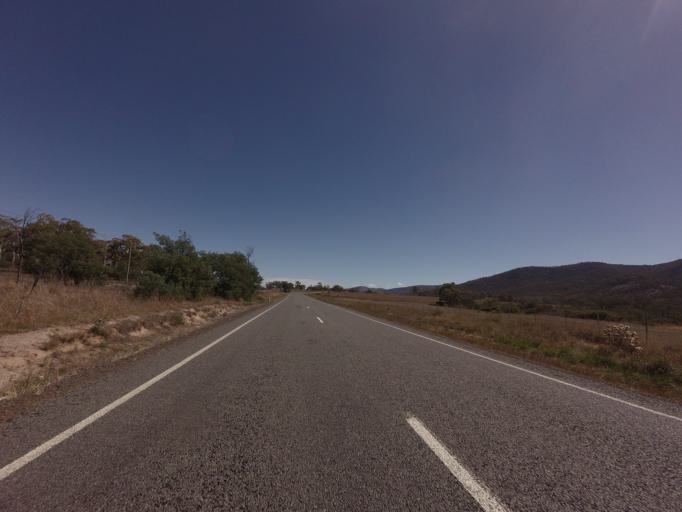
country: AU
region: Tasmania
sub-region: Northern Midlands
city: Evandale
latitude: -41.7512
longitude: 147.7760
